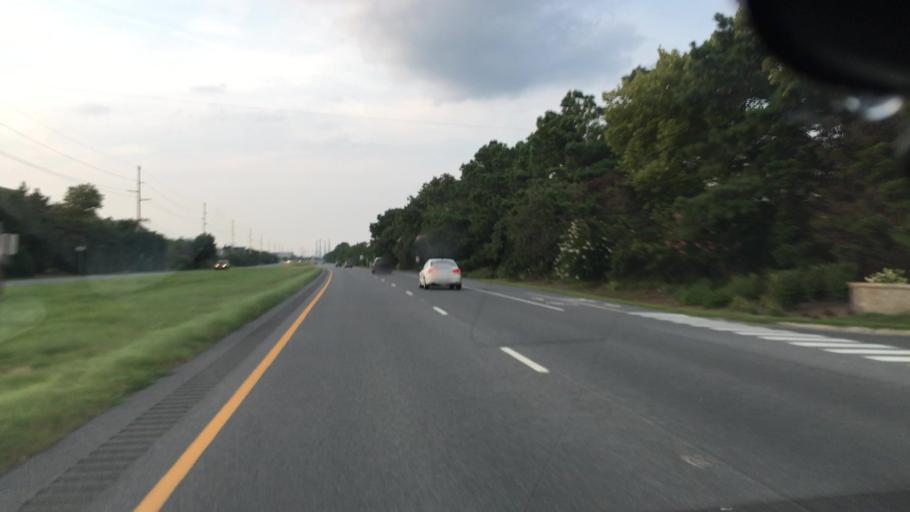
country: US
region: Delaware
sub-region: Sussex County
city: Bethany Beach
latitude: 38.5777
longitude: -75.0602
